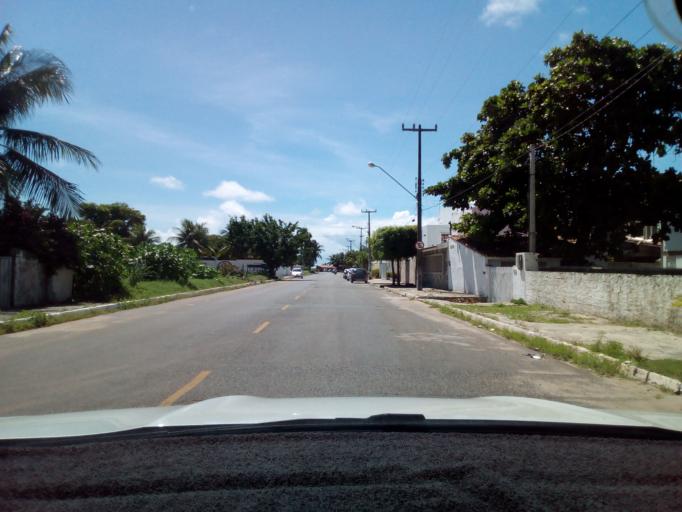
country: BR
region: Paraiba
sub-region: Joao Pessoa
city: Joao Pessoa
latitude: -7.1578
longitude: -34.7943
